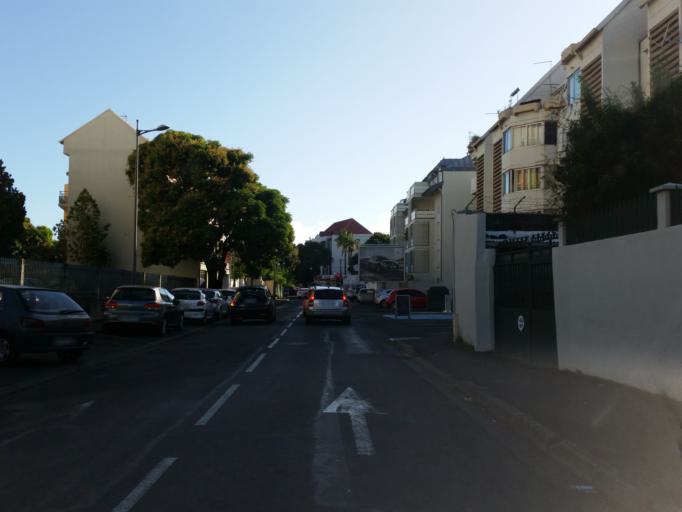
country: RE
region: Reunion
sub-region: Reunion
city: Saint-Denis
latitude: -20.8886
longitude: 55.4551
